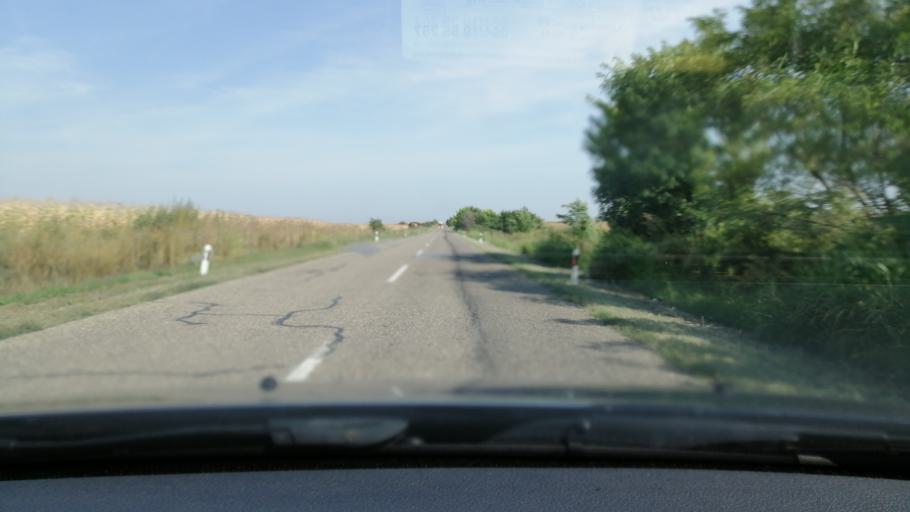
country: RS
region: Autonomna Pokrajina Vojvodina
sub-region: Juznobanatski Okrug
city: Kovacica
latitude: 45.1430
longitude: 20.6165
